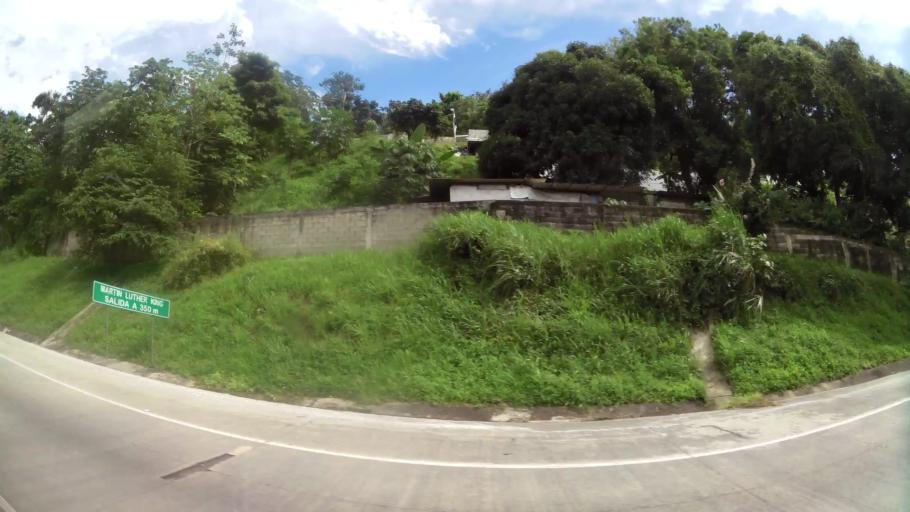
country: PA
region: Panama
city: San Miguelito
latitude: 9.0615
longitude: -79.5047
